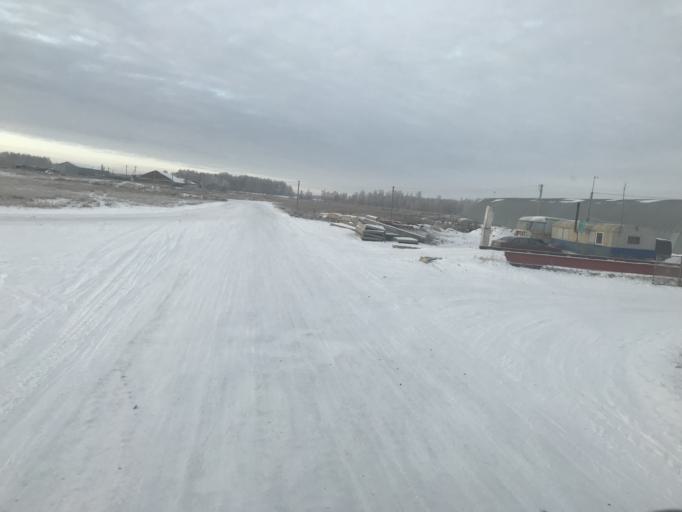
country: KZ
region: Soltustik Qazaqstan
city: Smirnovo
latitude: 54.8469
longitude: 69.7201
